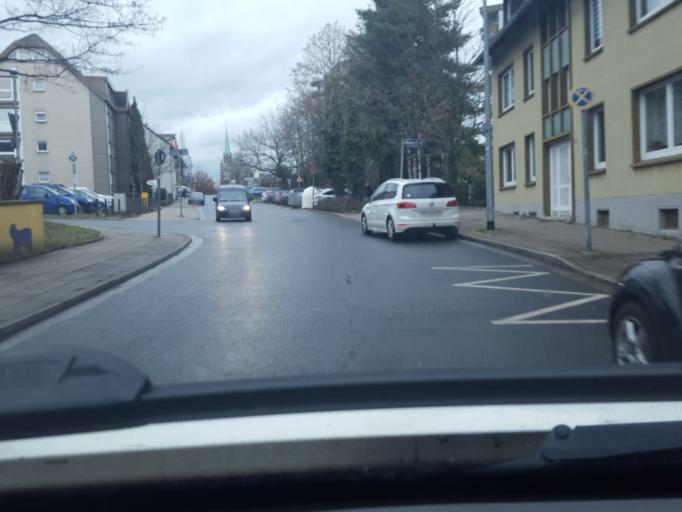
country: DE
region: North Rhine-Westphalia
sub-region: Regierungsbezirk Munster
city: Bottrop
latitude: 51.4705
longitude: 6.9529
